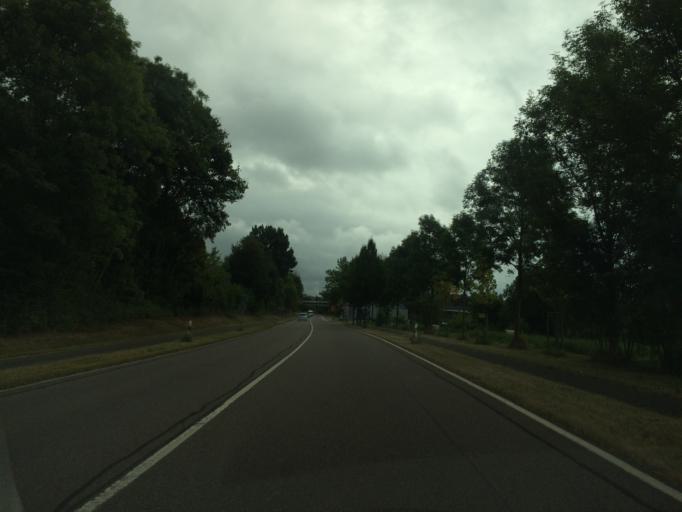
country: DE
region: Saarland
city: Merzig
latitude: 49.4114
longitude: 6.6449
